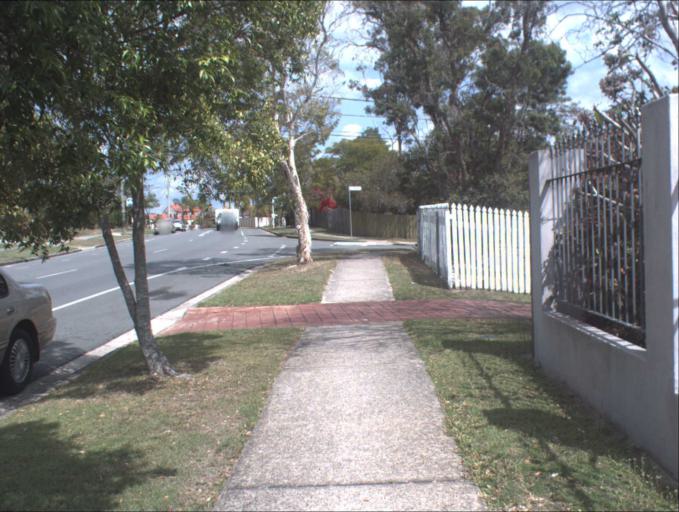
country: AU
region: Queensland
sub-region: Logan
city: Park Ridge South
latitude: -27.6685
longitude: 153.0383
